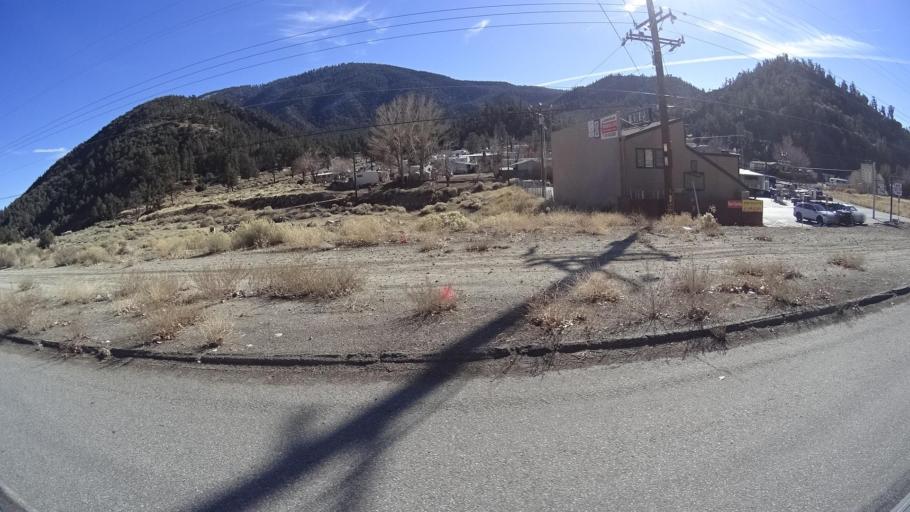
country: US
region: California
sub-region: Kern County
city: Frazier Park
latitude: 34.8192
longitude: -118.9914
